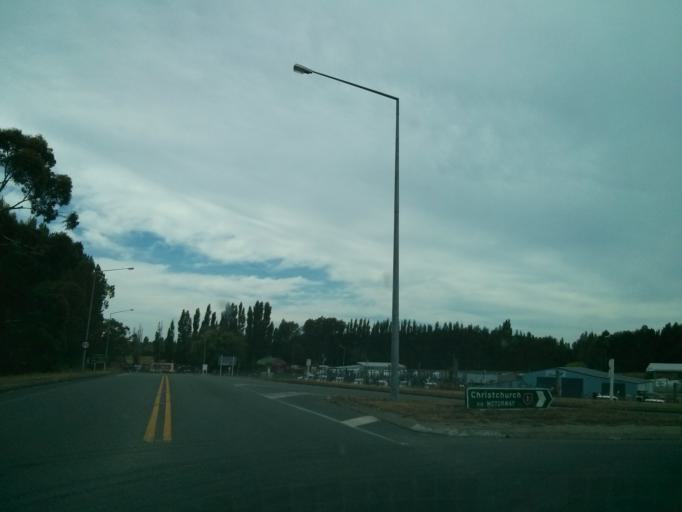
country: NZ
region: Canterbury
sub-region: Waimakariri District
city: Kaiapoi
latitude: -43.4079
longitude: 172.6452
